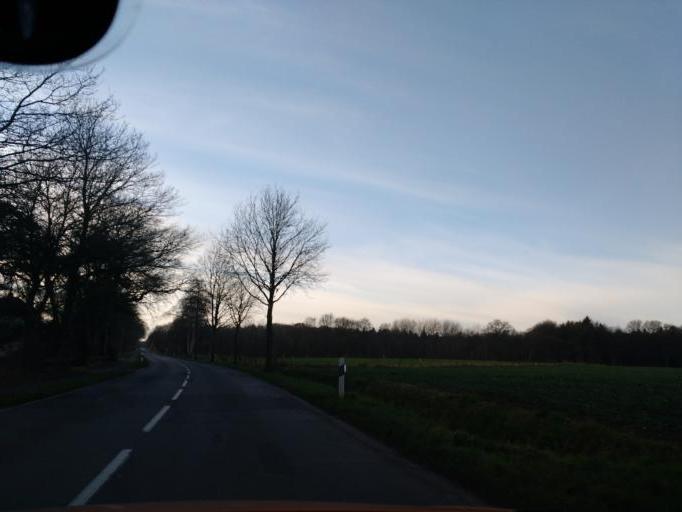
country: DE
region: Lower Saxony
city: Hude
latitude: 53.1155
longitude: 8.4453
